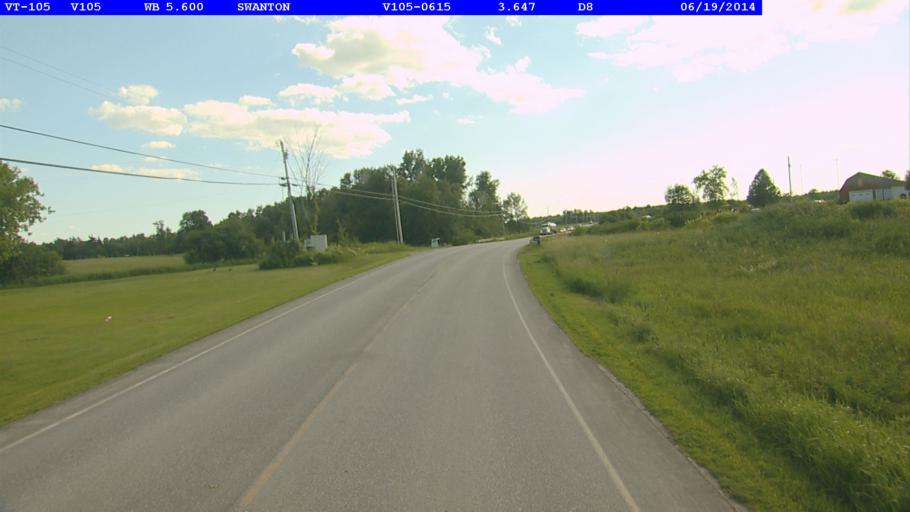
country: US
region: Vermont
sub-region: Franklin County
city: Saint Albans
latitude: 44.8820
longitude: -73.0226
